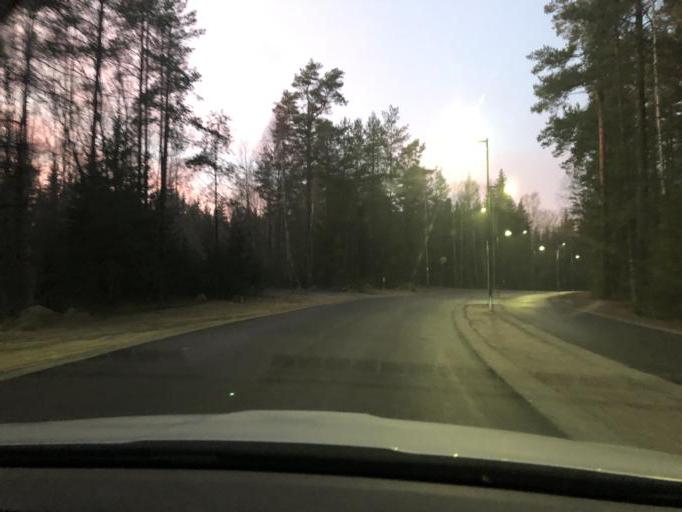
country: SE
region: Stockholm
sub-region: Botkyrka Kommun
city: Varsta
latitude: 59.1732
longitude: 17.7985
